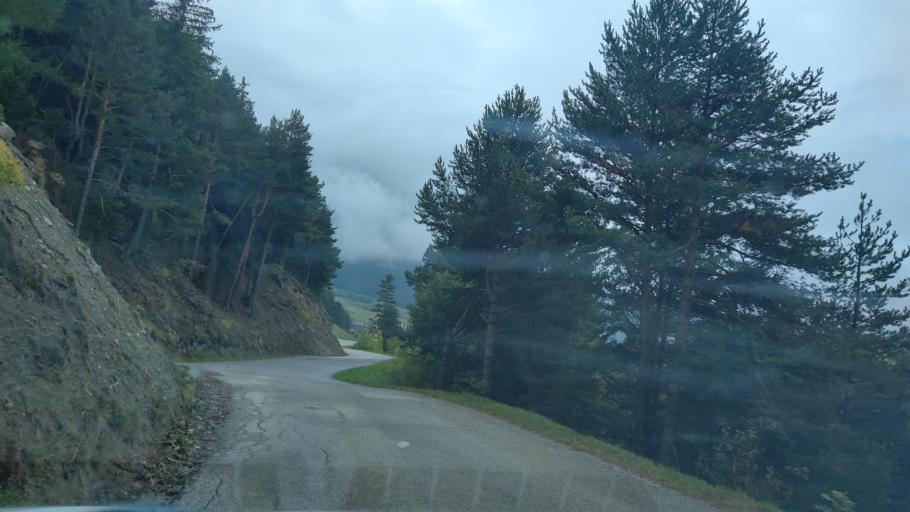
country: FR
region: Rhone-Alpes
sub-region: Departement de la Savoie
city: Modane
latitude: 45.2831
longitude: 6.8154
